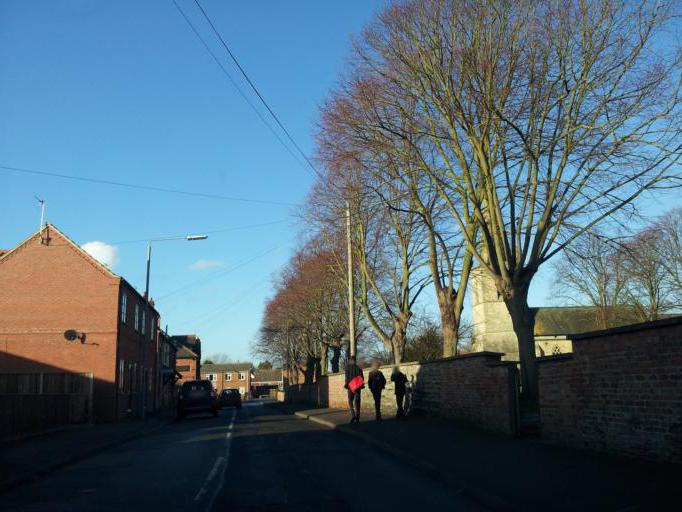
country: GB
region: England
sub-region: Nottinghamshire
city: Newark on Trent
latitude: 53.0545
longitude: -0.7788
